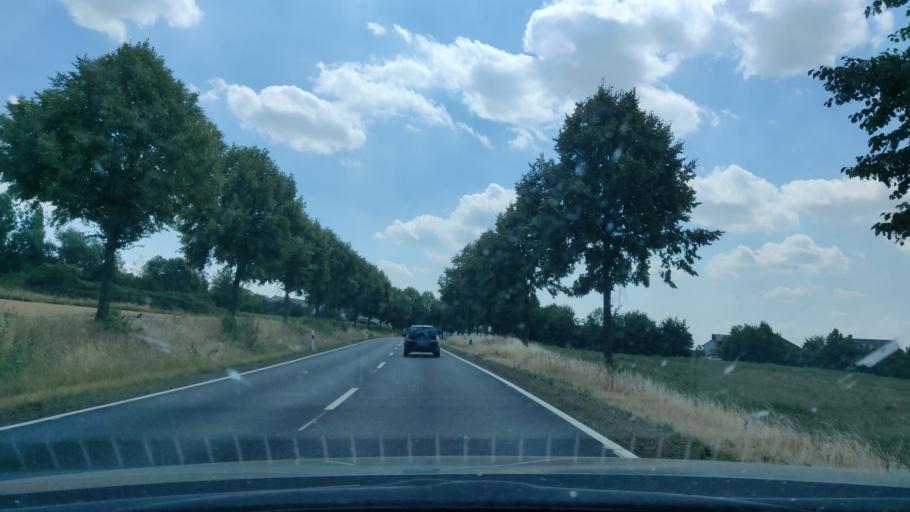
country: DE
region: Hesse
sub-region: Regierungsbezirk Kassel
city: Wabern
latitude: 51.0866
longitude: 9.3728
